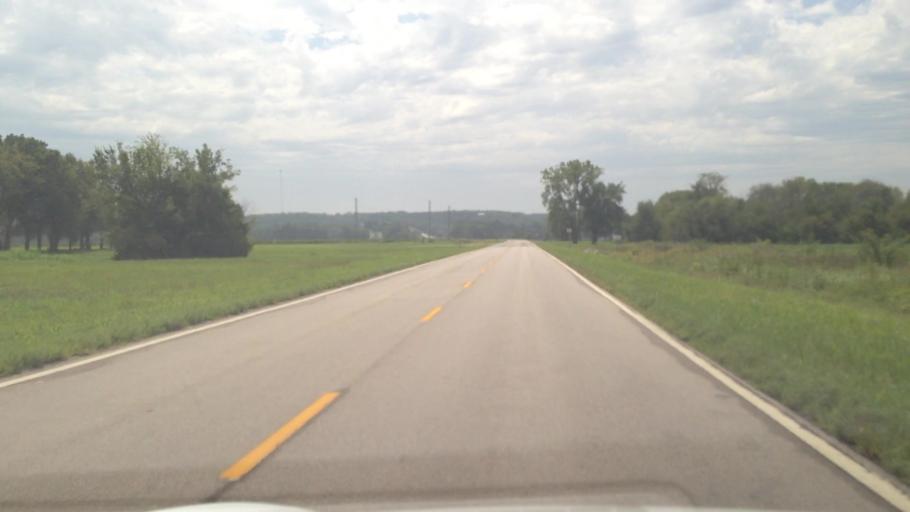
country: US
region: Kansas
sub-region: Bourbon County
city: Fort Scott
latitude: 37.8467
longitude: -94.9805
